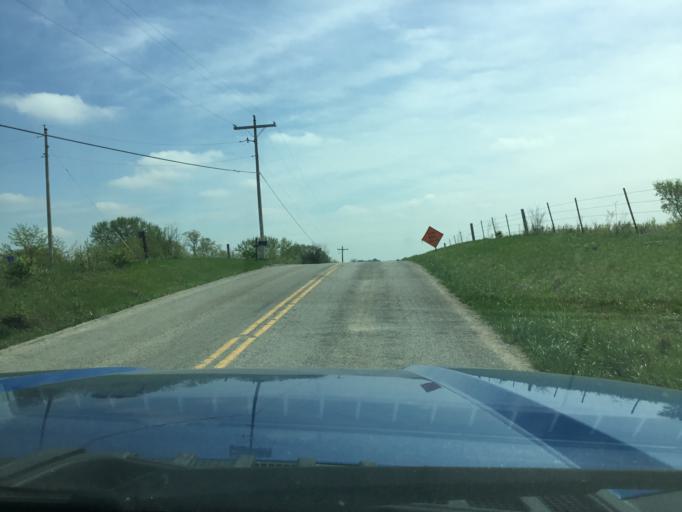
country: US
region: Kansas
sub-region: Shawnee County
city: Topeka
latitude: 39.1170
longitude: -95.5835
